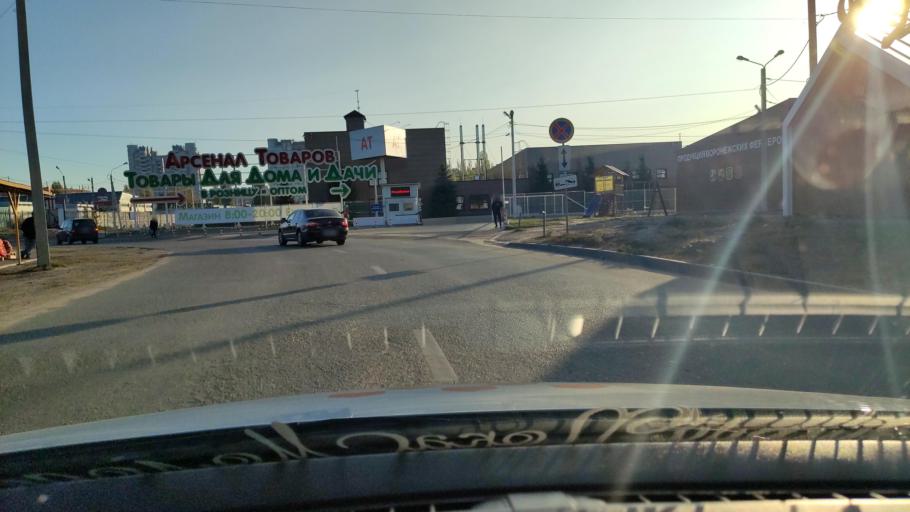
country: RU
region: Voronezj
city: Voronezh
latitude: 51.6428
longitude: 39.1366
